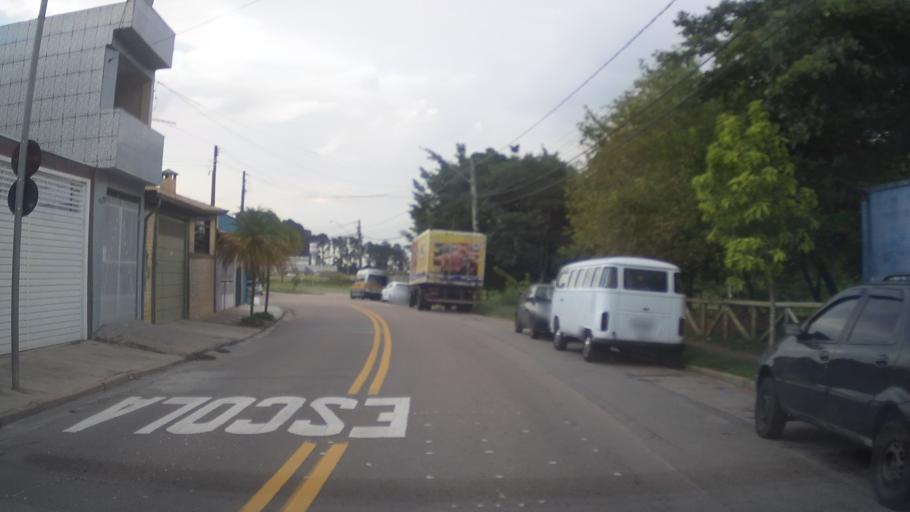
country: BR
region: Sao Paulo
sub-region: Jundiai
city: Jundiai
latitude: -23.1837
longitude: -46.9629
